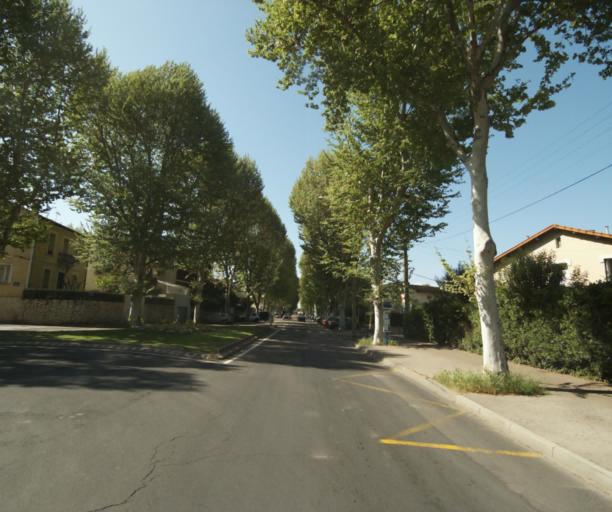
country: FR
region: Languedoc-Roussillon
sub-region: Departement de l'Herault
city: Montpellier
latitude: 43.6132
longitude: 3.8591
